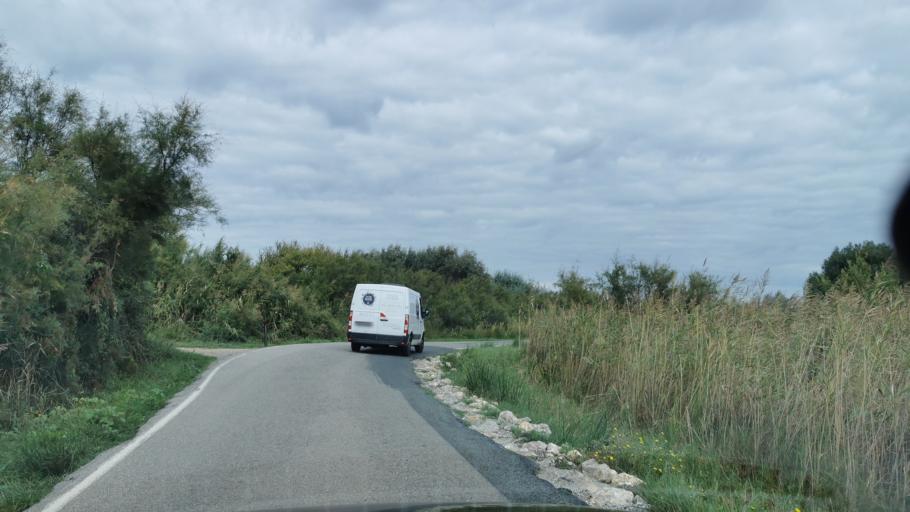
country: FR
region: Languedoc-Roussillon
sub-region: Departement de l'Aude
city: Fleury
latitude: 43.2139
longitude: 3.1943
